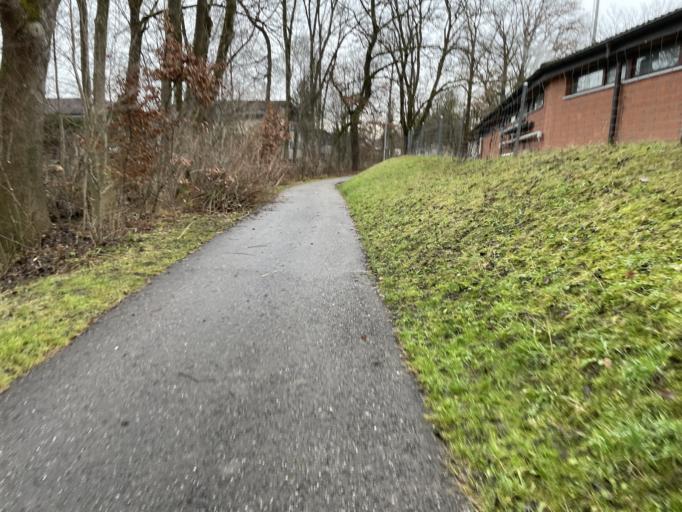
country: CH
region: Bern
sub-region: Bern-Mittelland District
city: Munsingen
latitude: 46.8686
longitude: 7.5499
